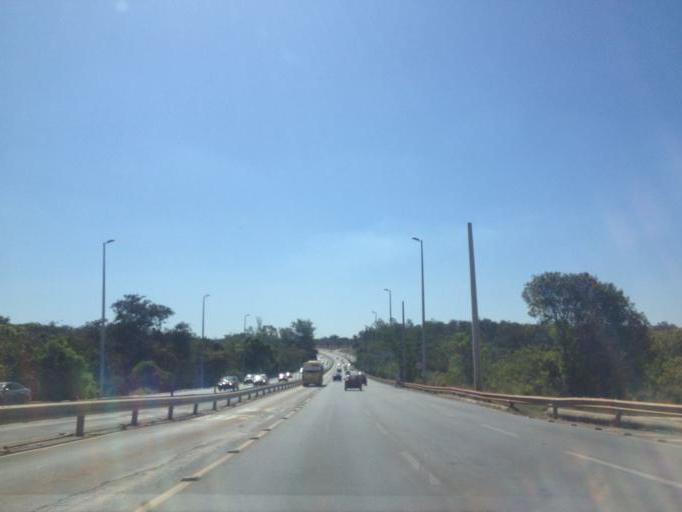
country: BR
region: Federal District
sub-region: Brasilia
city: Brasilia
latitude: -15.8553
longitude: -47.9333
